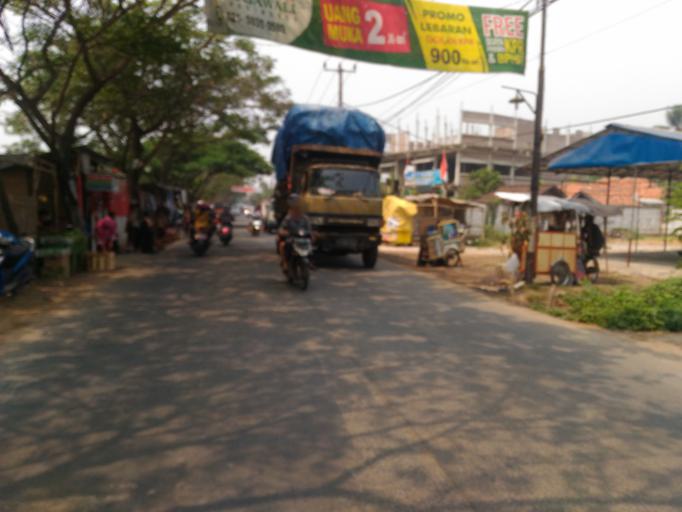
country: ID
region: West Java
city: Pasarkemis
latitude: -6.1403
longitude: 106.5449
